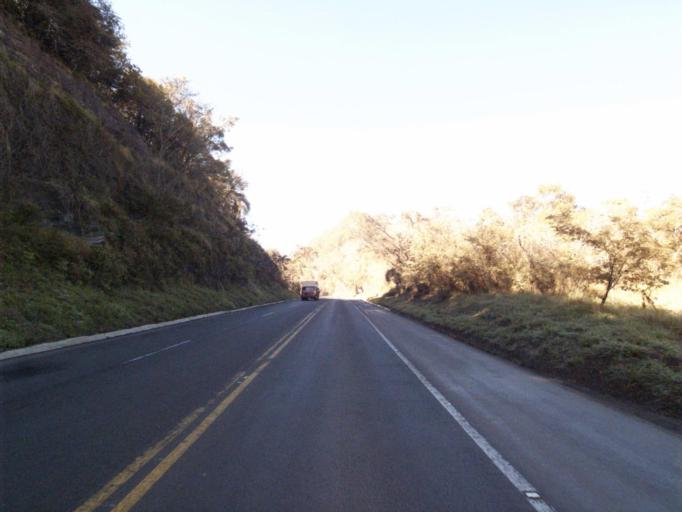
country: BR
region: Rio Grande do Sul
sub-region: Frederico Westphalen
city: Frederico Westphalen
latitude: -26.8187
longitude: -53.4282
